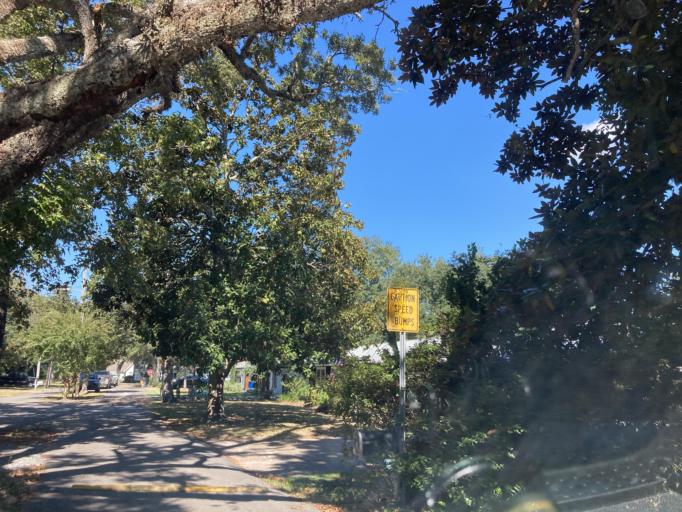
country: US
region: Mississippi
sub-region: Jackson County
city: Ocean Springs
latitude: 30.4100
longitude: -88.8360
